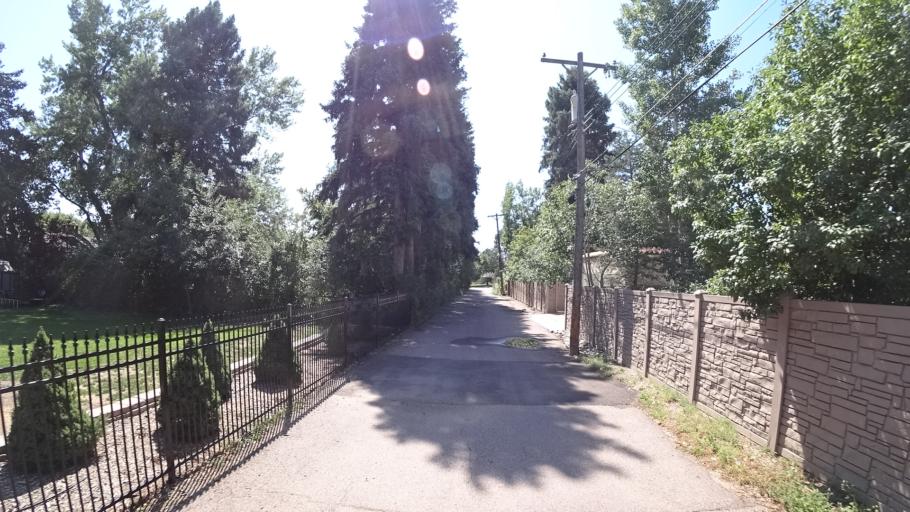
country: US
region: Colorado
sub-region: El Paso County
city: Colorado Springs
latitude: 38.8568
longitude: -104.8300
